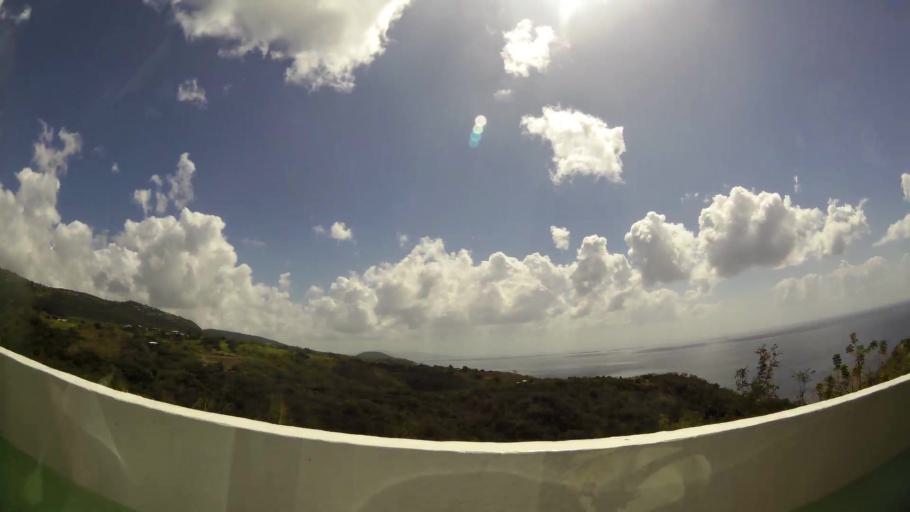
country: MQ
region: Martinique
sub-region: Martinique
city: Saint-Pierre
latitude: 14.6924
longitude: -61.1734
